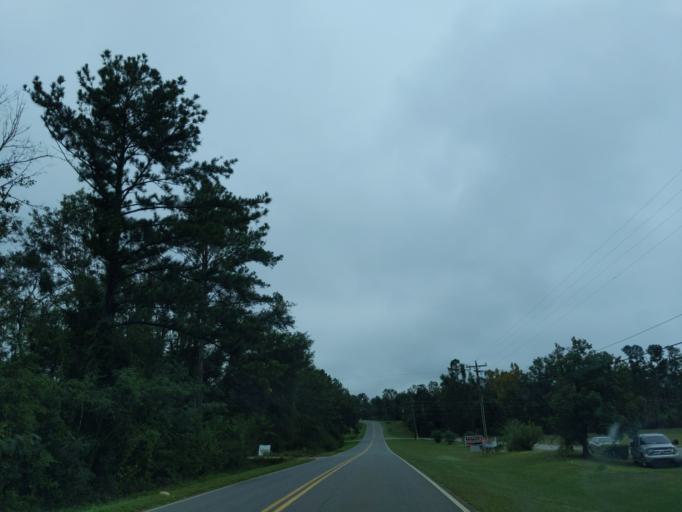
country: US
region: Florida
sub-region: Jackson County
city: Sneads
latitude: 30.7283
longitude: -84.9370
